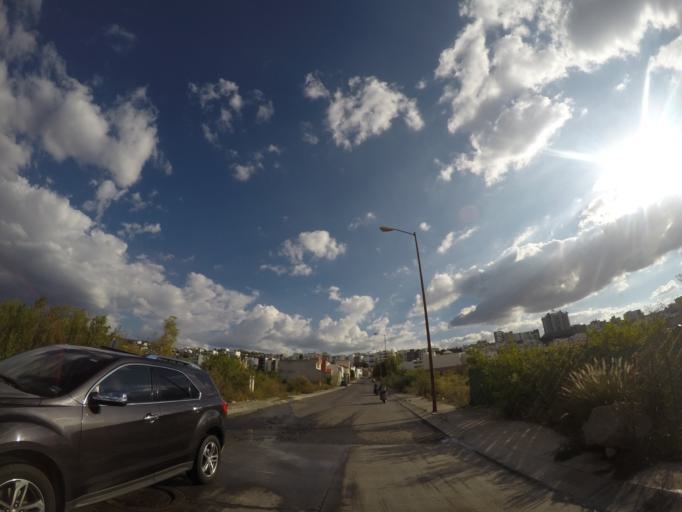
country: MX
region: San Luis Potosi
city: Escalerillas
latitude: 22.1257
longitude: -101.0273
